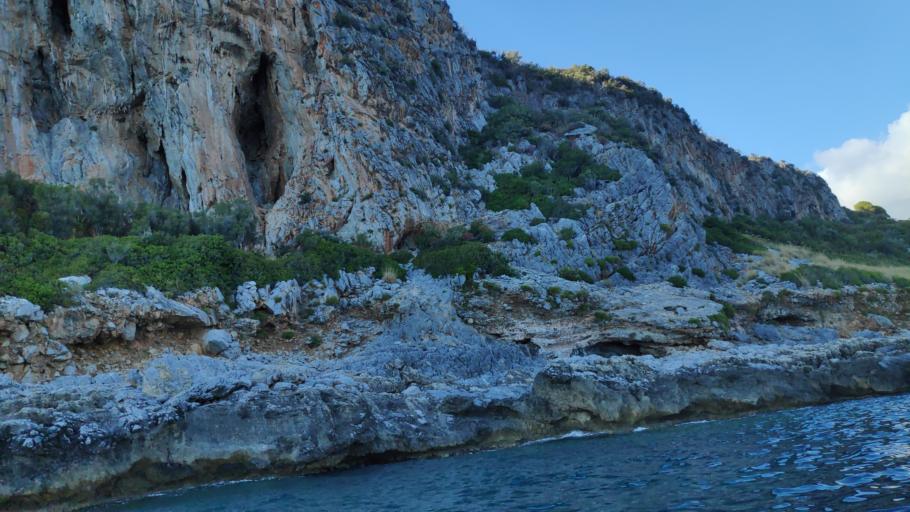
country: IT
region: Calabria
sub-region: Provincia di Cosenza
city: Praia a Mare
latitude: 39.8715
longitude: 15.7720
